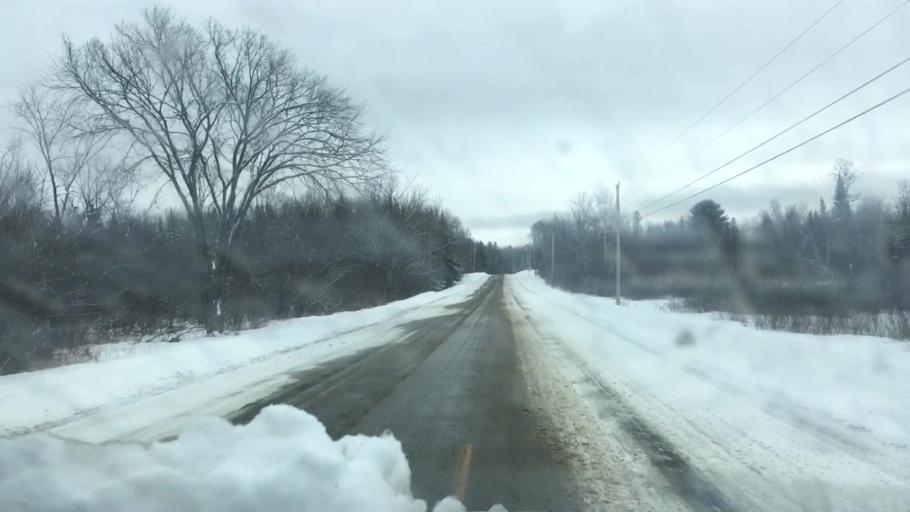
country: US
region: Maine
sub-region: Penobscot County
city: Hudson
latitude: 45.0239
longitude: -68.9203
